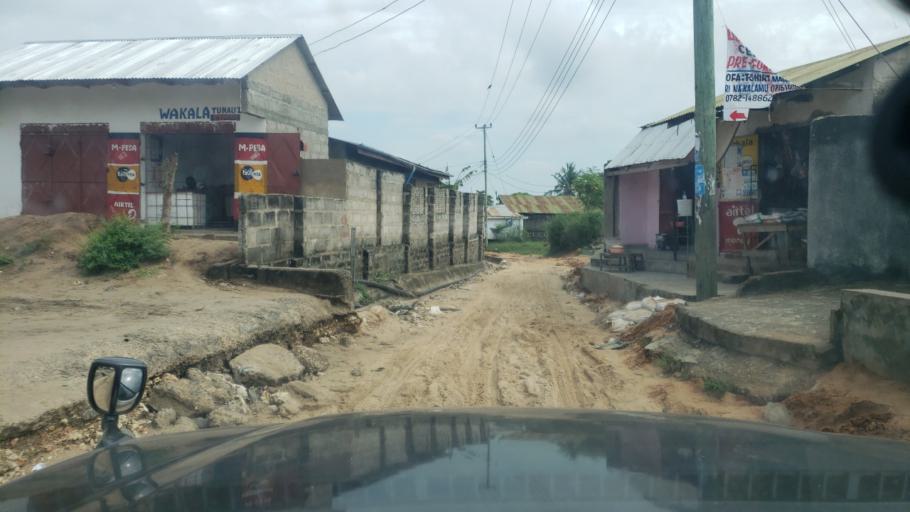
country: TZ
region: Pwani
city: Vikindu
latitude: -6.9219
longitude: 39.2549
